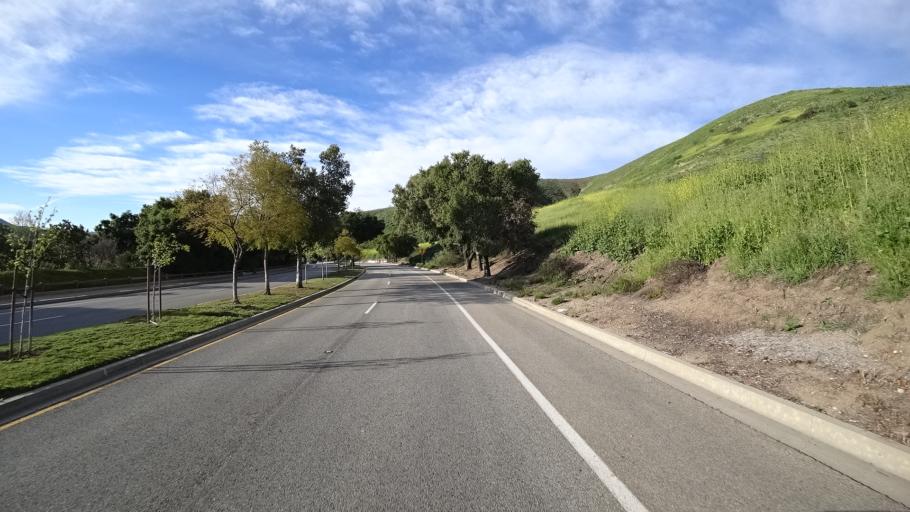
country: US
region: California
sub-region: Ventura County
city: Thousand Oaks
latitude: 34.1932
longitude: -118.8239
